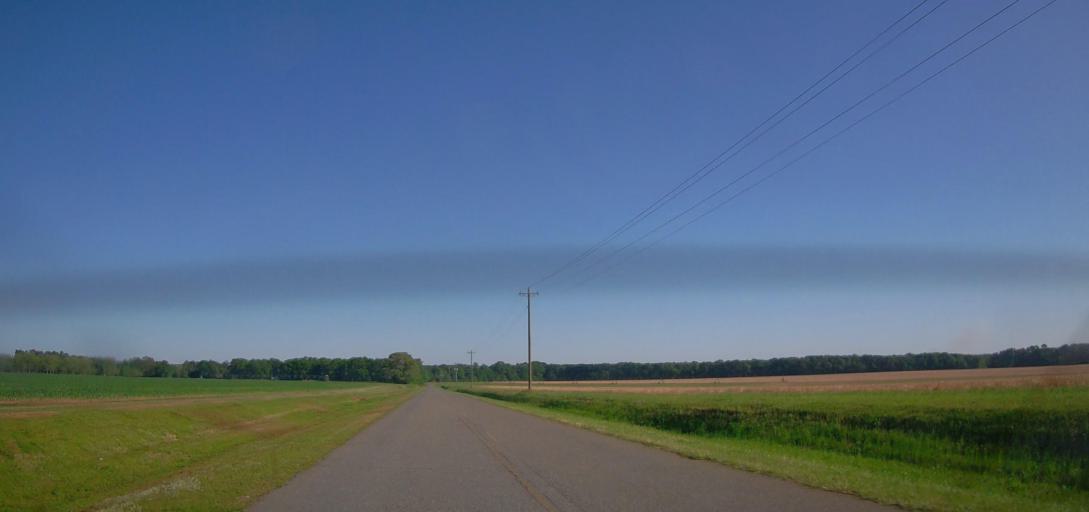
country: US
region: Georgia
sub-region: Houston County
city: Perry
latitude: 32.4262
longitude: -83.7797
